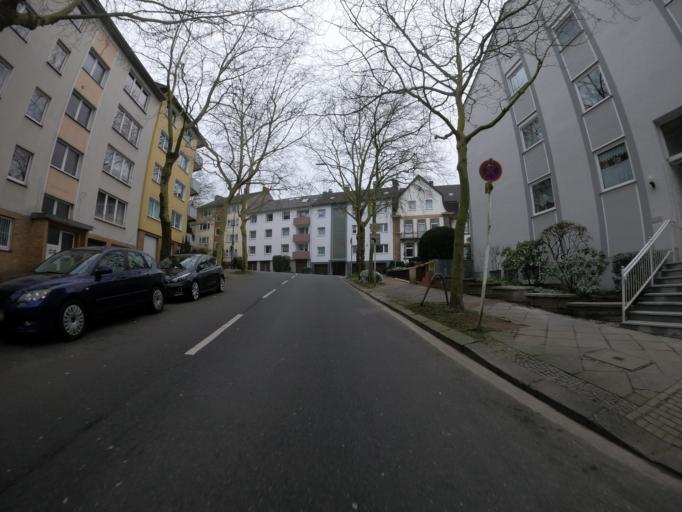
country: DE
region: North Rhine-Westphalia
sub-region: Regierungsbezirk Dusseldorf
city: Wuppertal
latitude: 51.2488
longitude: 7.1526
